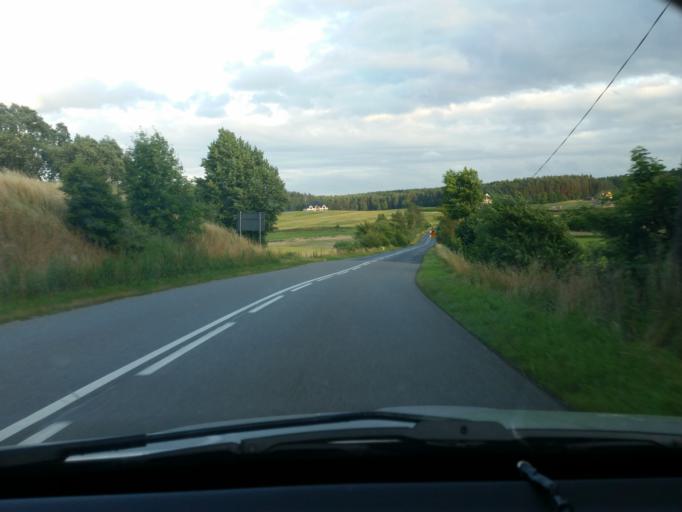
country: PL
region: Pomeranian Voivodeship
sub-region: Powiat czluchowski
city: Przechlewo
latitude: 53.8177
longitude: 17.4090
